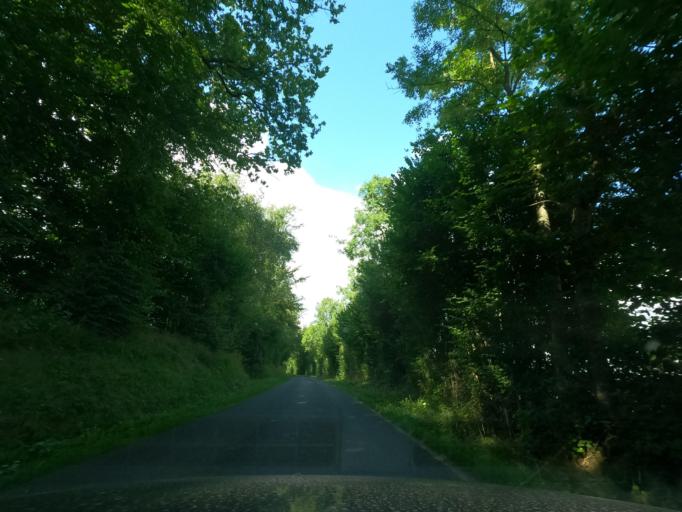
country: FR
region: Lower Normandy
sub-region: Departement de l'Orne
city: Gace
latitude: 48.7764
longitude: 0.2581
